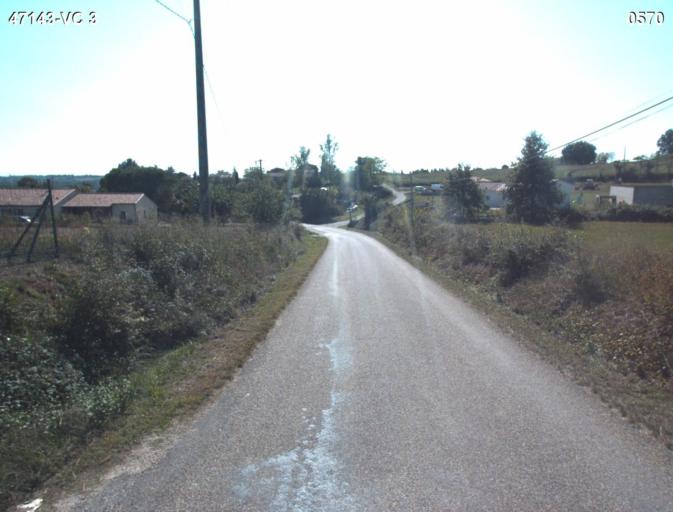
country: FR
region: Aquitaine
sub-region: Departement du Lot-et-Garonne
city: Lavardac
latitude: 44.1886
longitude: 0.2951
